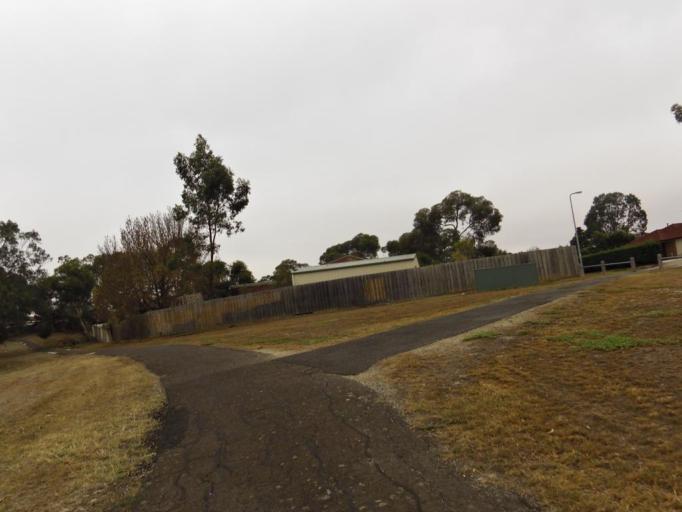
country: AU
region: Victoria
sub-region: Melton
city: Kurunjang
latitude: -37.6713
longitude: 144.5956
